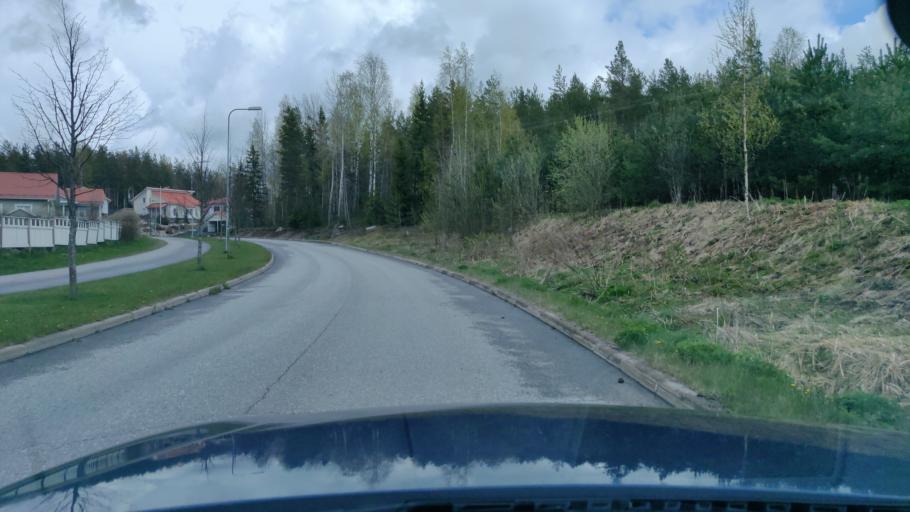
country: FI
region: Uusimaa
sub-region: Helsinki
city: Nurmijaervi
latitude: 60.3632
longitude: 24.7268
